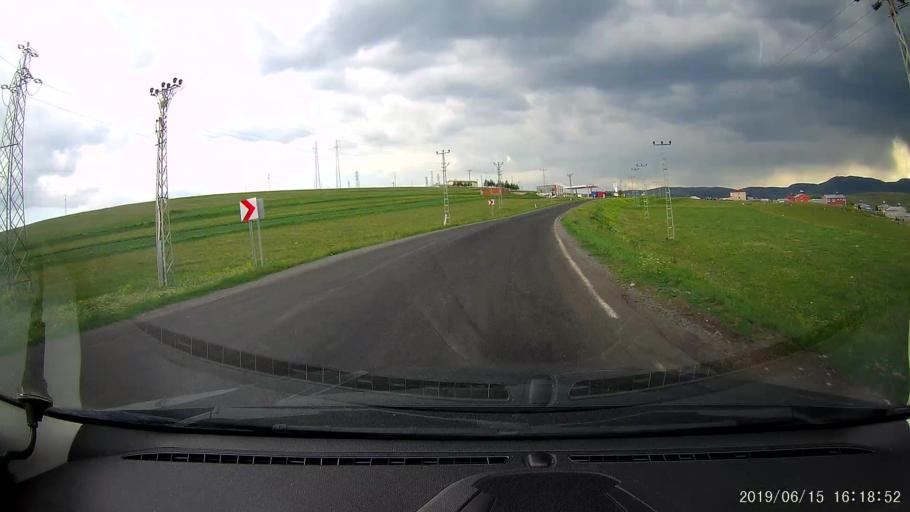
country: TR
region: Ardahan
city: Hanak
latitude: 41.2345
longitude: 42.8529
